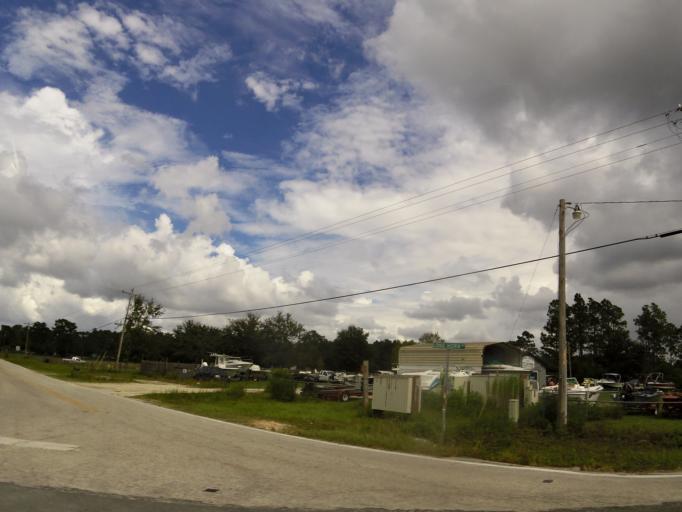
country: US
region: Florida
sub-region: Clay County
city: Middleburg
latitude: 30.1081
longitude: -81.9616
